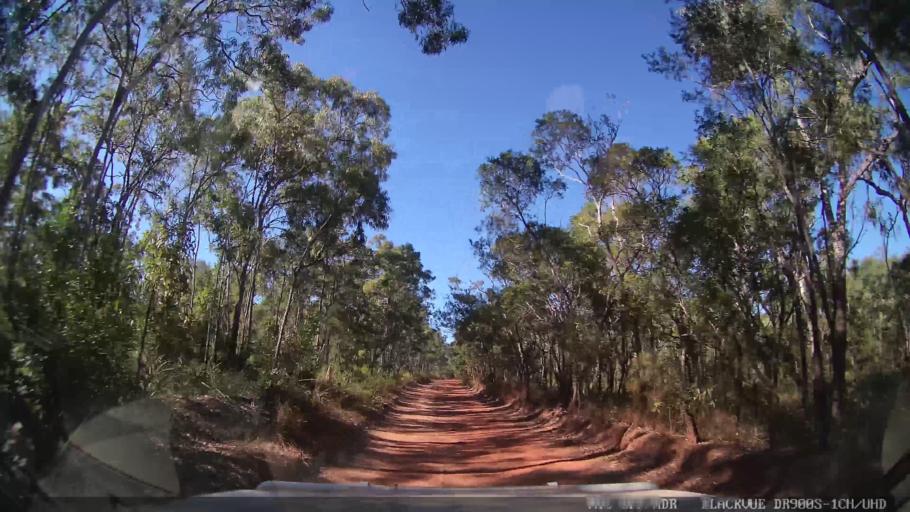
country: AU
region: Queensland
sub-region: Torres
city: Thursday Island
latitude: -11.4070
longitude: 142.4078
